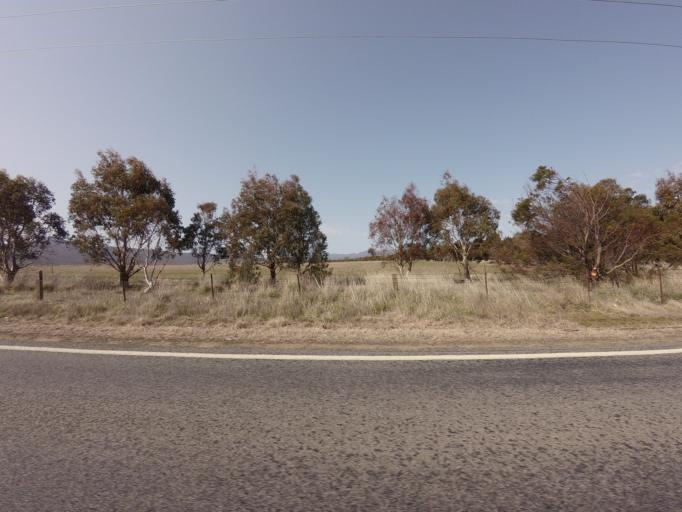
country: AU
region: Tasmania
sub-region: Northern Midlands
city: Evandale
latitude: -41.7944
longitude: 147.7088
